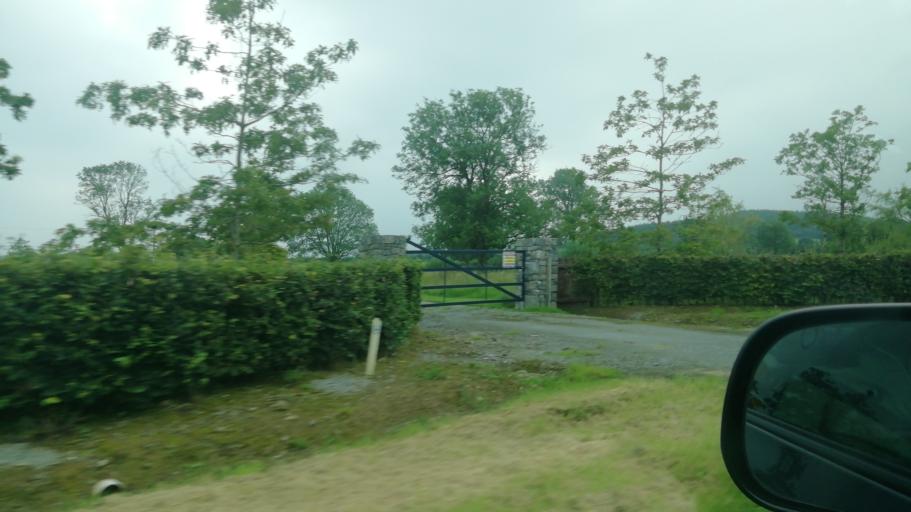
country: IE
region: Munster
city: Fethard
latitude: 52.4903
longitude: -7.6912
